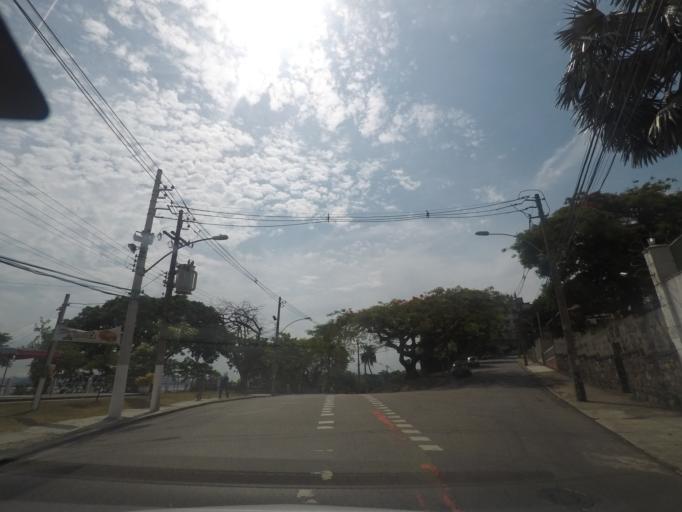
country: BR
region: Rio de Janeiro
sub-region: Rio De Janeiro
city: Rio de Janeiro
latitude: -22.8200
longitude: -43.1905
